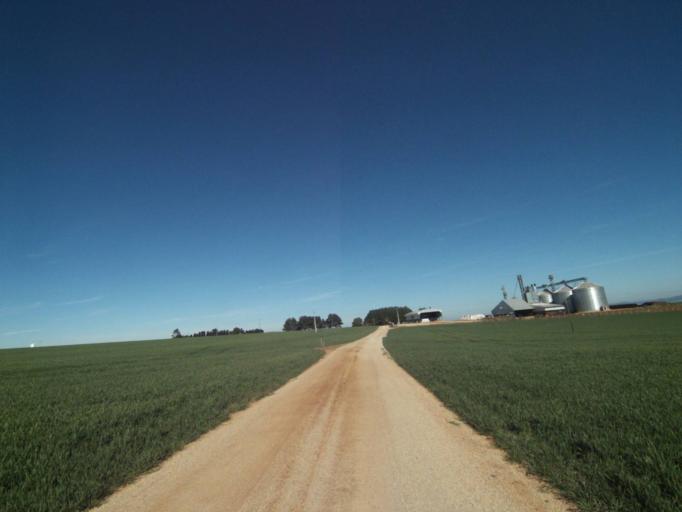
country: BR
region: Parana
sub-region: Tibagi
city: Tibagi
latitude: -24.5396
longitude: -50.3037
